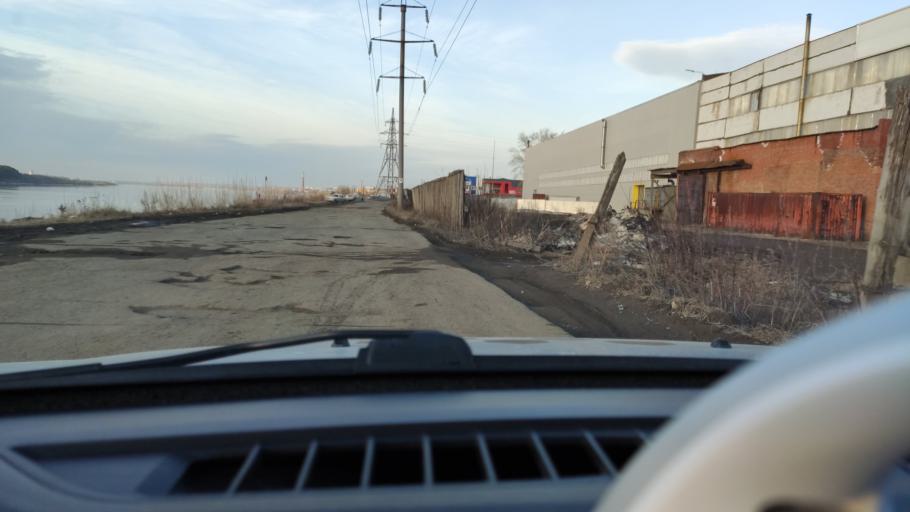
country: RU
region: Perm
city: Perm
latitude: 58.0411
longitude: 56.3064
